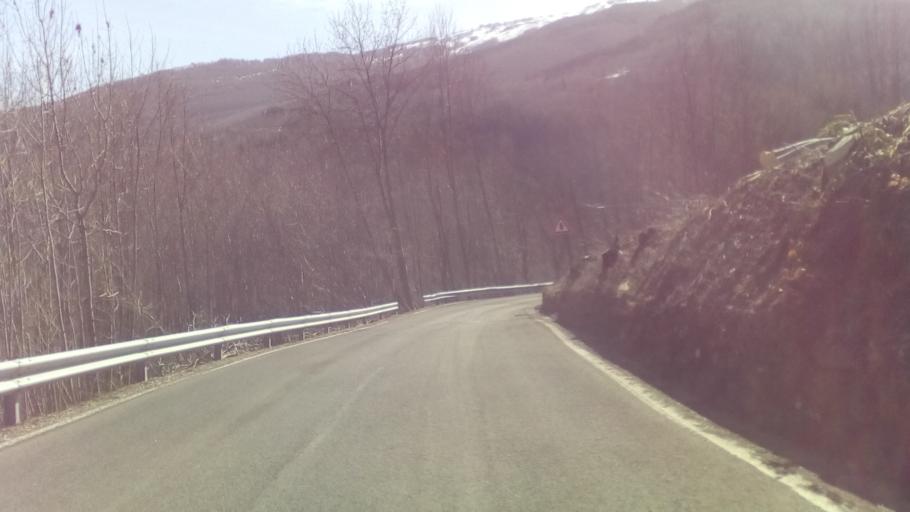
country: IT
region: Emilia-Romagna
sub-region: Provincia di Modena
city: Pievepelago
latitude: 44.1897
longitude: 10.5610
